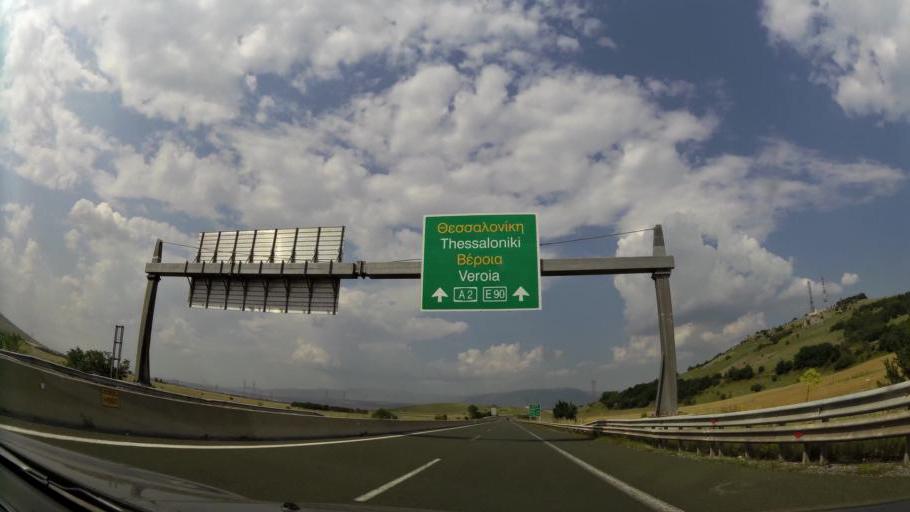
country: GR
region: West Macedonia
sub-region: Nomos Kozanis
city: Koila
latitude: 40.3550
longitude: 21.8126
